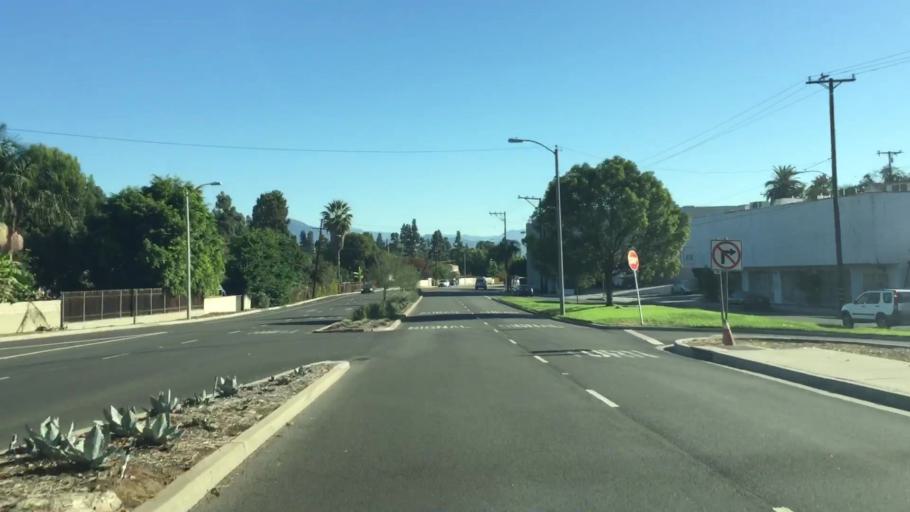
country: US
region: California
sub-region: Los Angeles County
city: Monterey Park
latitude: 34.0611
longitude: -118.1422
